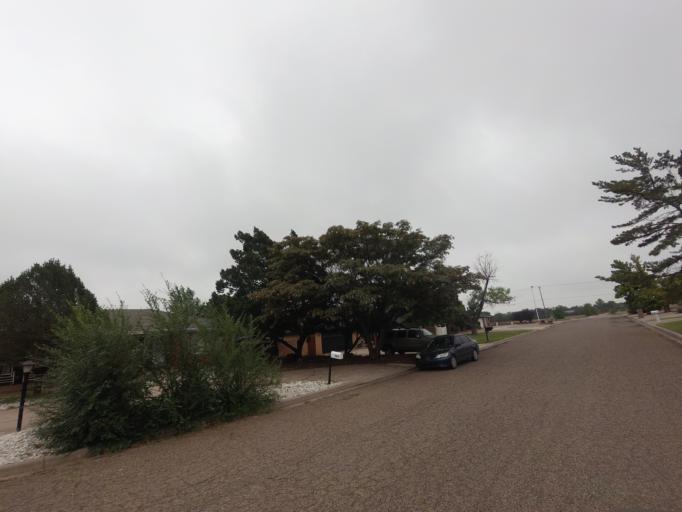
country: US
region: New Mexico
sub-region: Curry County
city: Clovis
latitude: 34.4347
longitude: -103.1906
